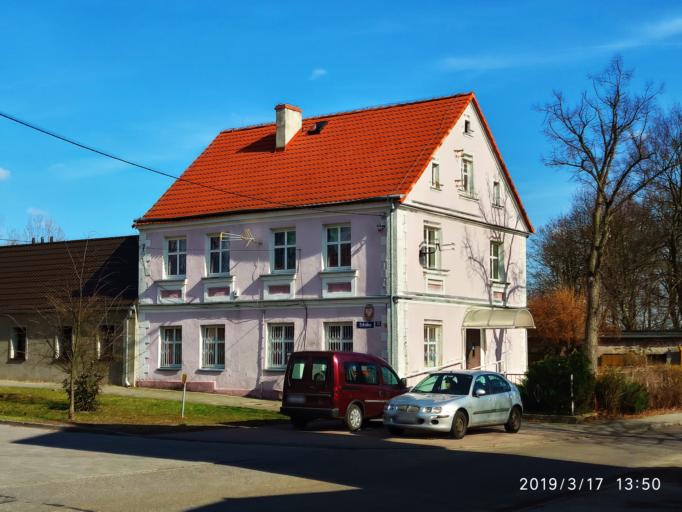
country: PL
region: Lubusz
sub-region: Powiat zielonogorski
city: Zabor
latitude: 51.9500
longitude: 15.7159
